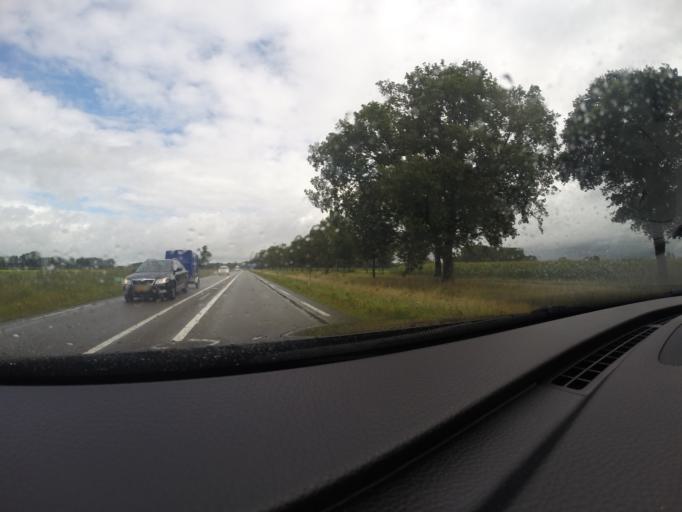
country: NL
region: Gelderland
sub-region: Gemeente Lochem
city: Laren
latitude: 52.2619
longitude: 6.4014
